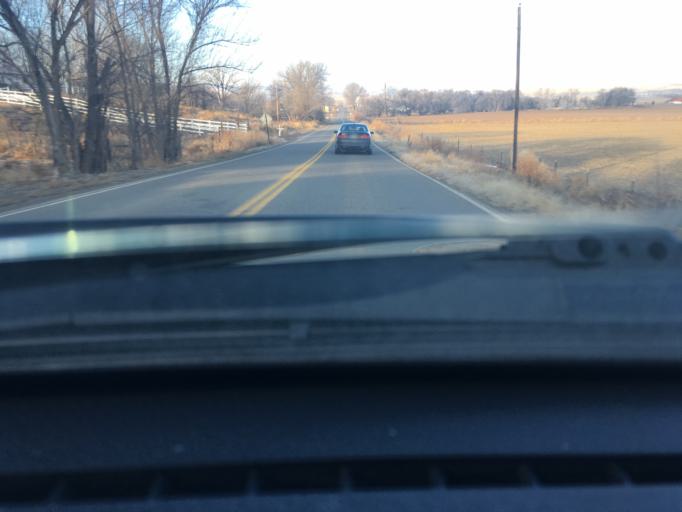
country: US
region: Colorado
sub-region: Delta County
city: Delta
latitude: 38.7410
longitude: -108.0947
